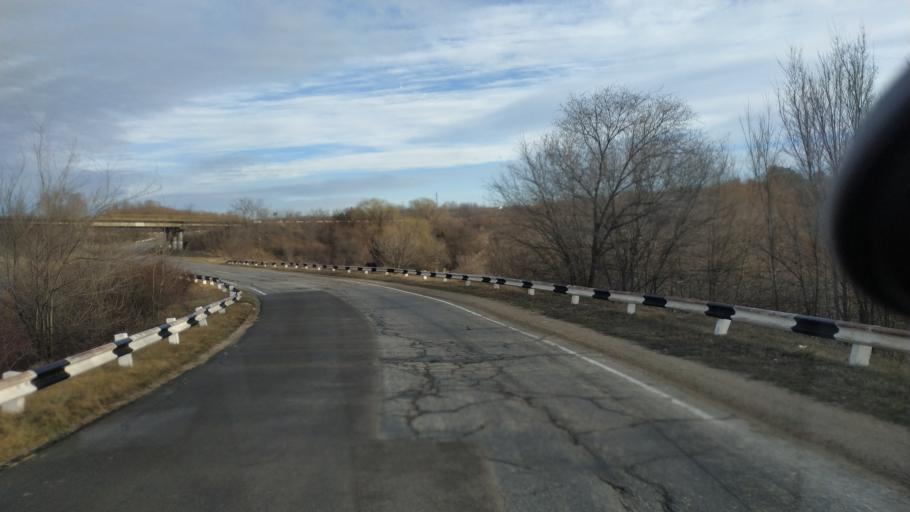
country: MD
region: Chisinau
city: Vadul lui Voda
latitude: 47.0700
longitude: 29.0205
